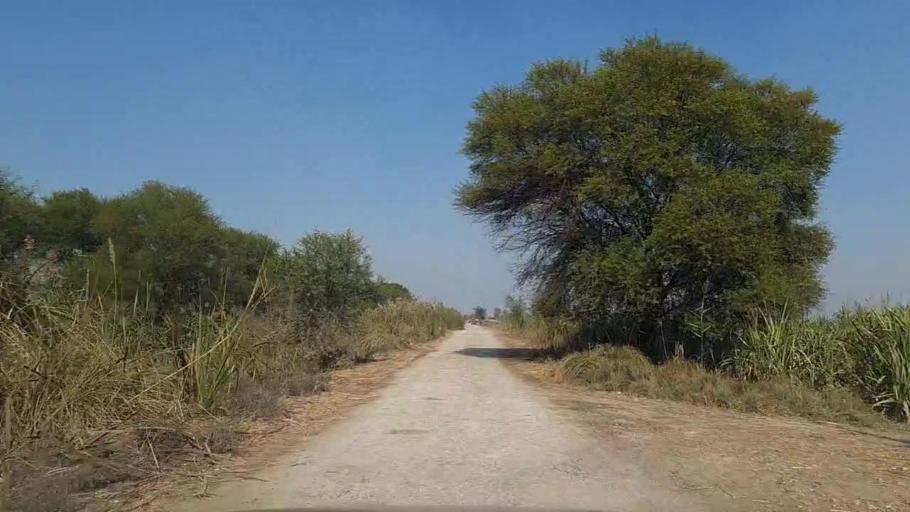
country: PK
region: Sindh
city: Daur
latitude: 26.5024
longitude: 68.3463
